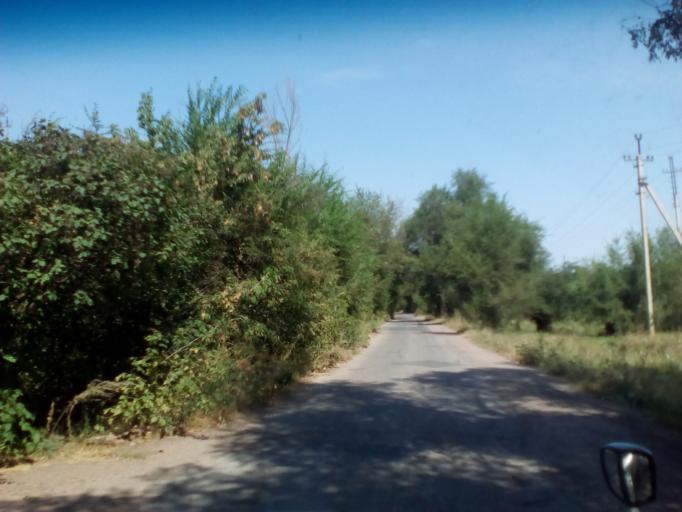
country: KZ
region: Almaty Oblysy
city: Burunday
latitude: 43.1609
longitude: 76.3876
